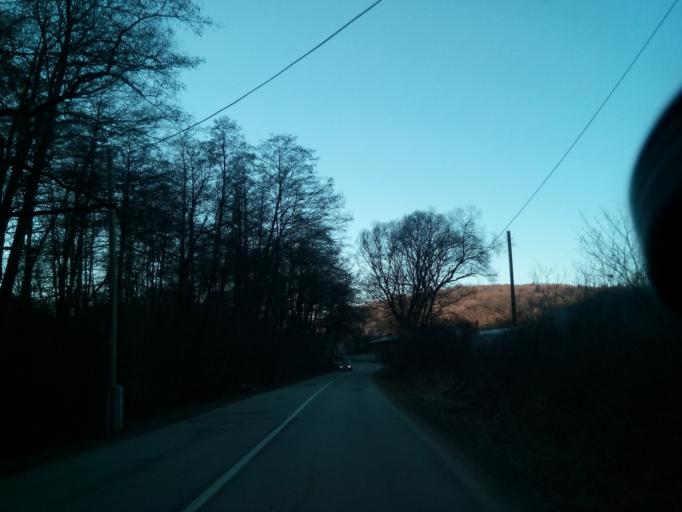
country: SK
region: Kosicky
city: Medzev
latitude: 48.6937
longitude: 20.9471
